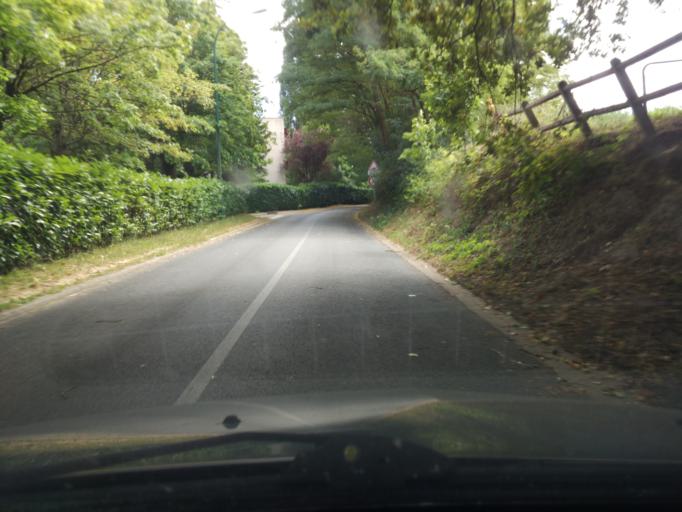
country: FR
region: Ile-de-France
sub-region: Departement de l'Essonne
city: Villiers-le-Bacle
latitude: 48.7085
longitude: 2.1206
